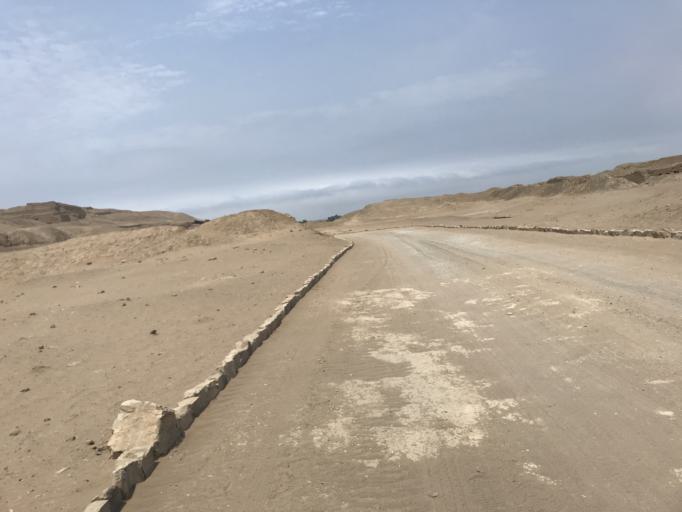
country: PE
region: Lima
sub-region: Lima
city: Punta Hermosa
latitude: -12.2579
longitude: -76.8979
